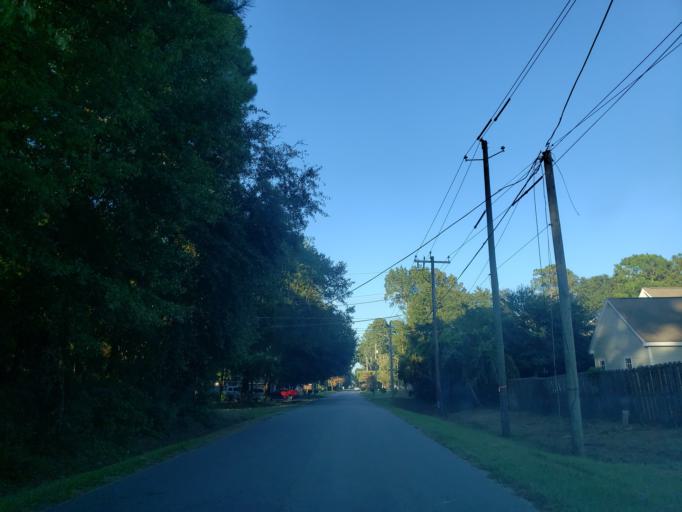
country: US
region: Georgia
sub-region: Chatham County
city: Isle of Hope
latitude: 31.9955
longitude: -81.0682
